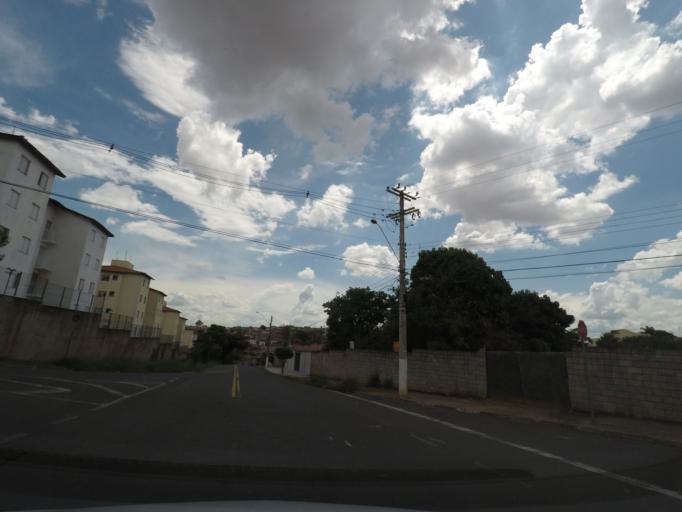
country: BR
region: Sao Paulo
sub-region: Campinas
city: Campinas
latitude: -22.9252
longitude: -47.0187
